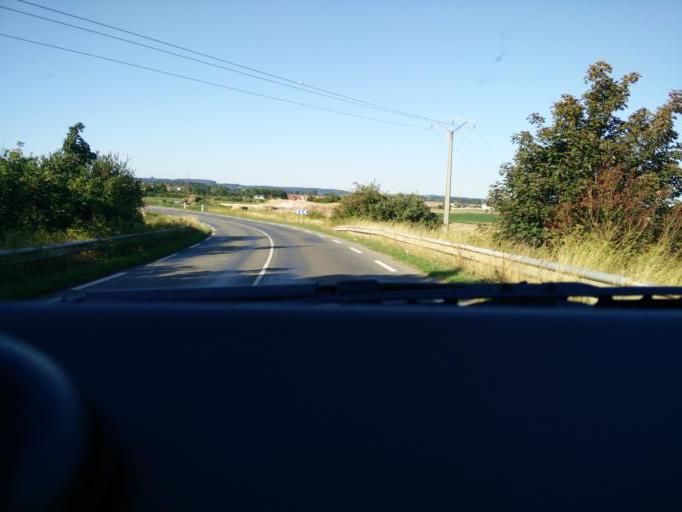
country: FR
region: Nord-Pas-de-Calais
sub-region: Departement du Pas-de-Calais
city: Sains-en-Gohelle
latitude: 50.4577
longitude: 2.6943
